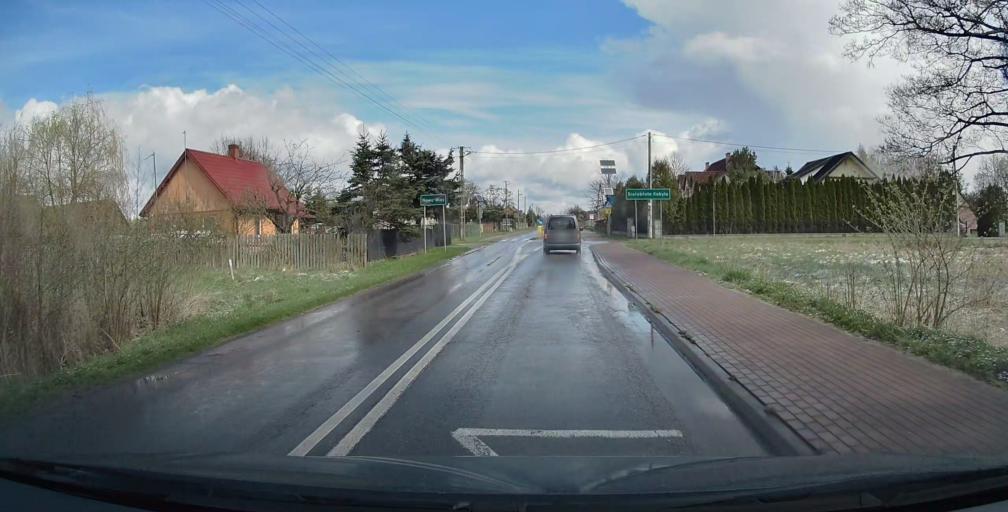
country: PL
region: Masovian Voivodeship
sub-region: Powiat wyszkowski
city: Branszczyk
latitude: 52.6939
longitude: 21.5995
